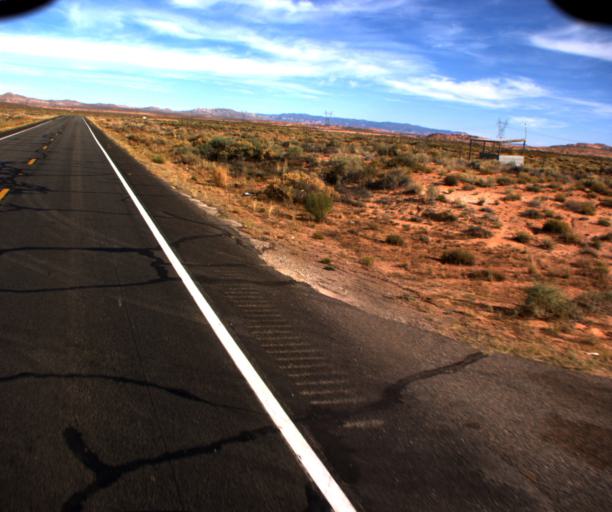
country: US
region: Arizona
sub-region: Apache County
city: Many Farms
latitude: 36.9414
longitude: -109.6553
